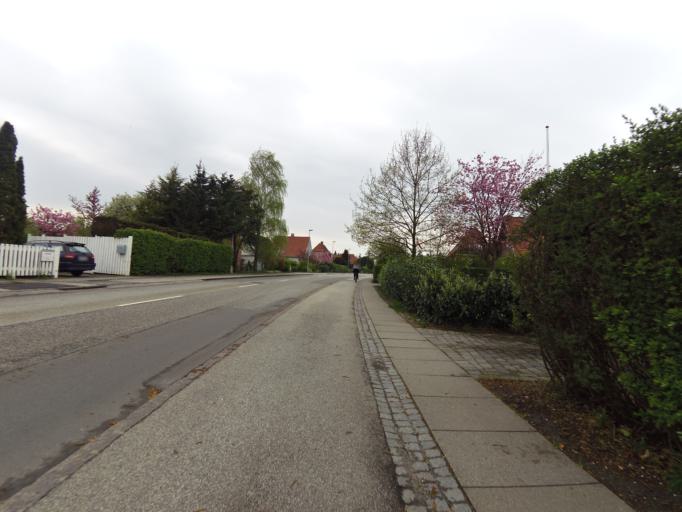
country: DK
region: Capital Region
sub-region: Lyngby-Tarbaek Kommune
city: Kongens Lyngby
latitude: 55.7316
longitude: 12.5314
